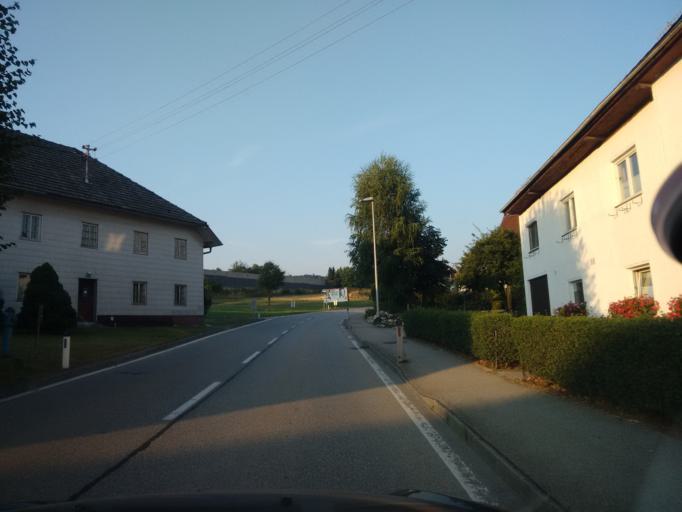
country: AT
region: Upper Austria
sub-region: Politischer Bezirk Grieskirchen
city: Bad Schallerbach
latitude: 48.1874
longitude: 13.9124
